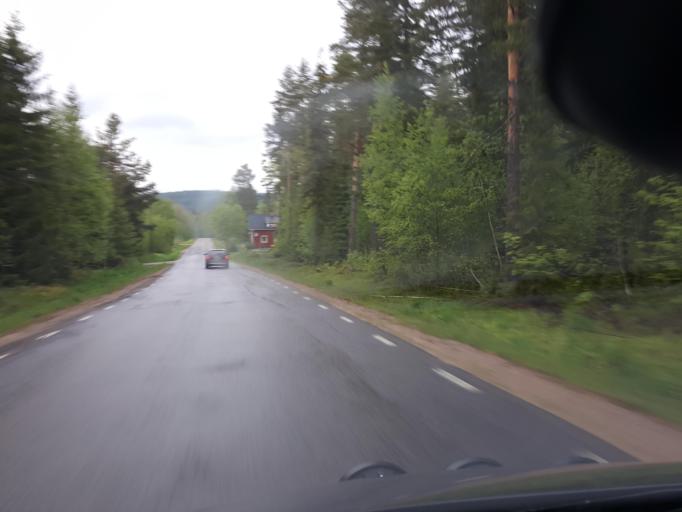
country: SE
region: Gaevleborg
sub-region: Ljusdals Kommun
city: Jaervsoe
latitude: 61.7850
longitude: 16.2172
